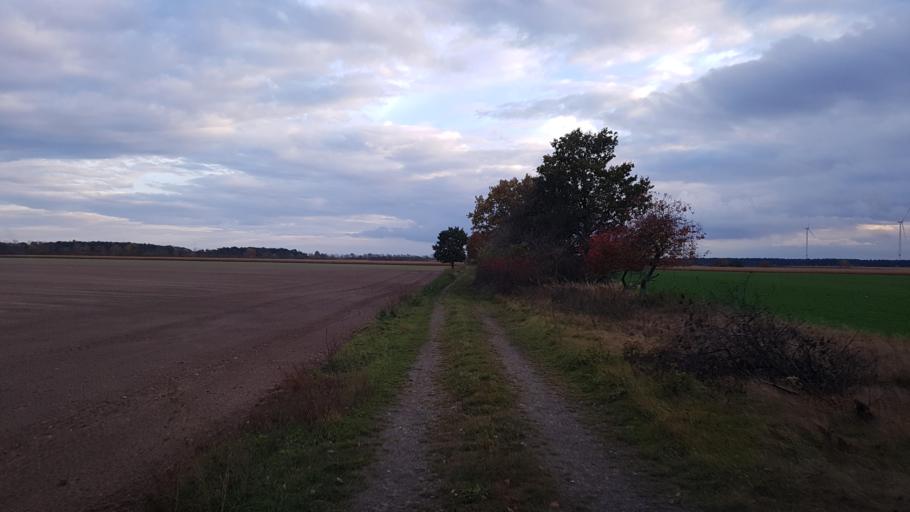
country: DE
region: Saxony-Anhalt
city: Seyda
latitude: 51.9398
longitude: 12.8751
